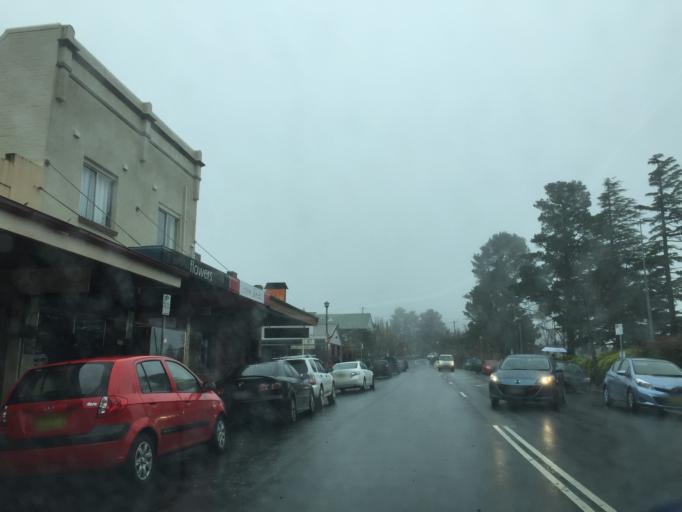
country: AU
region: New South Wales
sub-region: Blue Mountains Municipality
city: Leura
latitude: -33.7096
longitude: 150.3759
